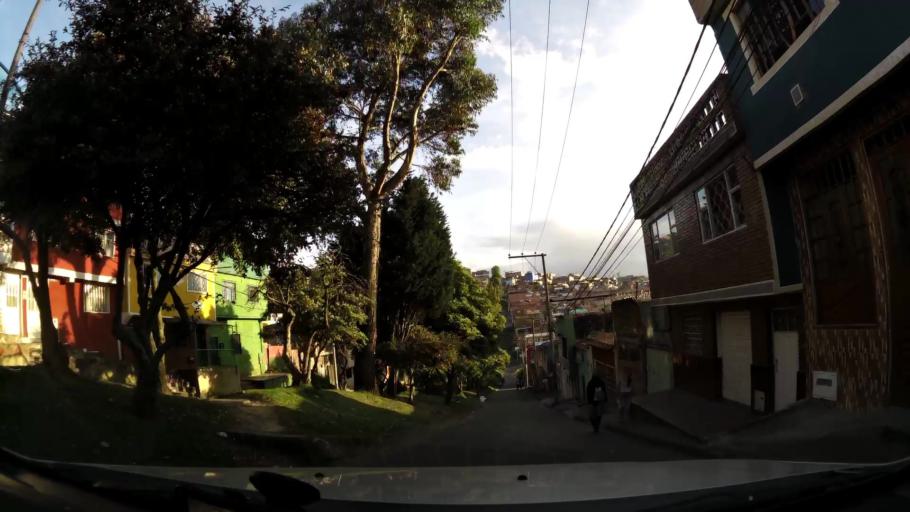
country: CO
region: Bogota D.C.
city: Bogota
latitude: 4.5433
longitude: -74.0886
